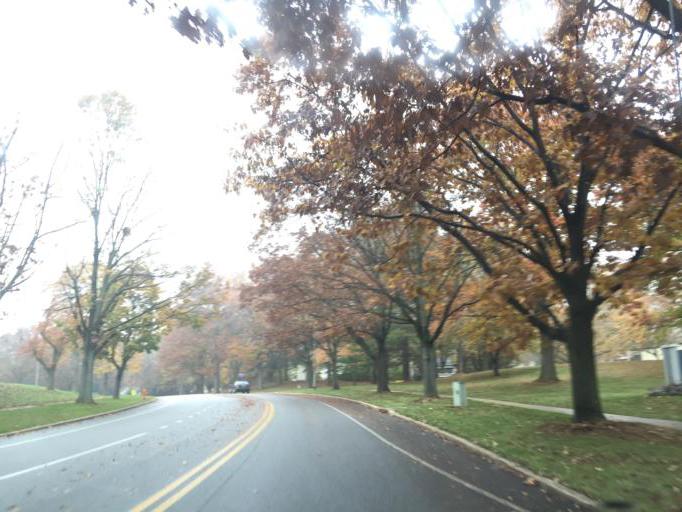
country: US
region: Maryland
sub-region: Howard County
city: Columbia
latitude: 39.1940
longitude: -76.8394
